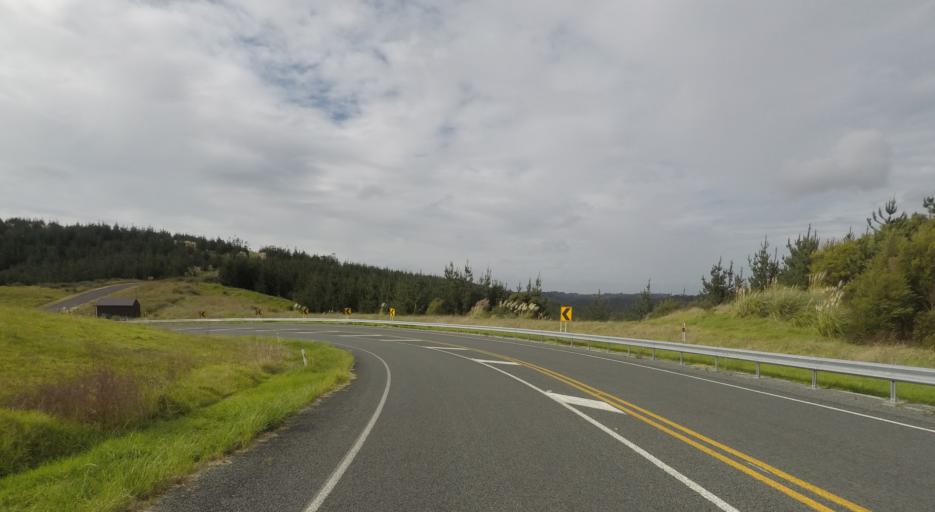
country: NZ
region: Auckland
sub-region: Auckland
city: Rothesay Bay
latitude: -36.6560
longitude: 174.6984
